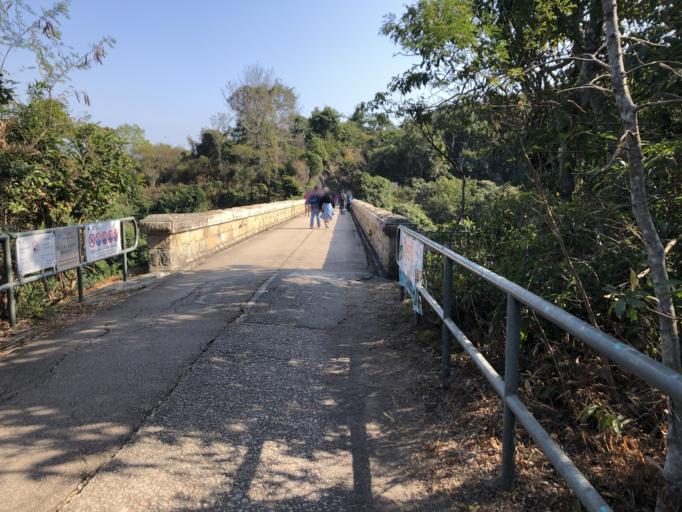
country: HK
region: Wanchai
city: Wan Chai
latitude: 22.2488
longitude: 114.2136
